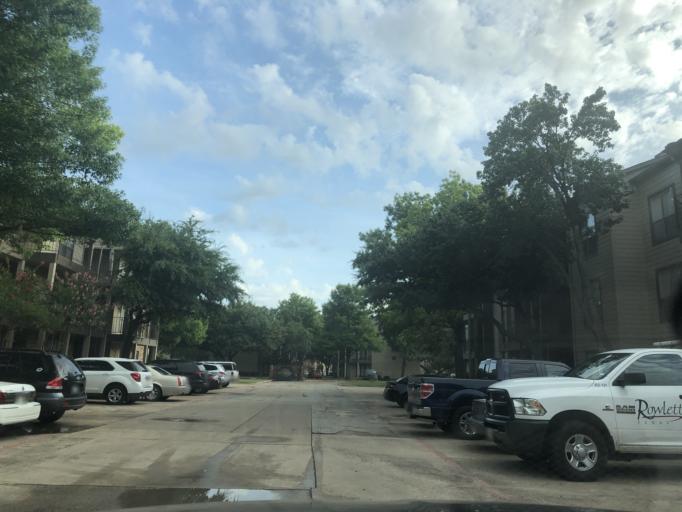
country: US
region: Texas
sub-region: Dallas County
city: Sunnyvale
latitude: 32.8490
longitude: -96.5769
